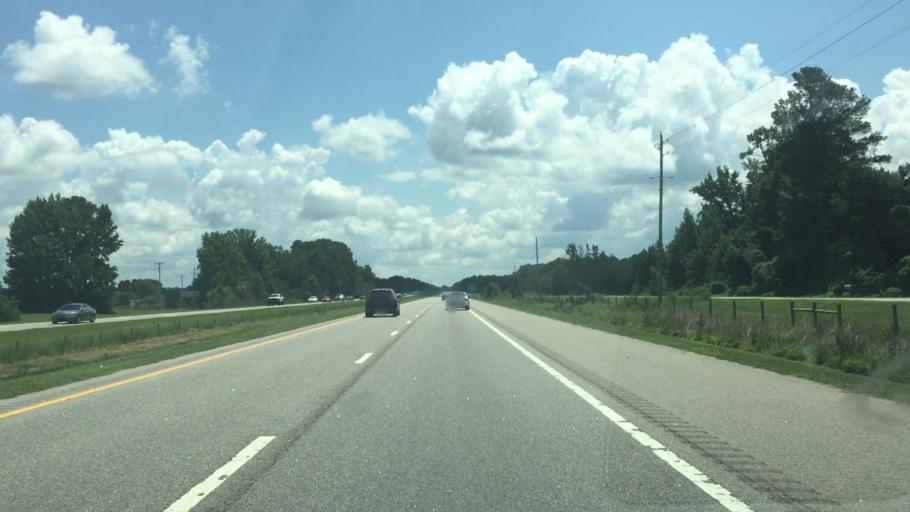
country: US
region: North Carolina
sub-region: Robeson County
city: Lumberton
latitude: 34.5848
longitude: -79.0579
